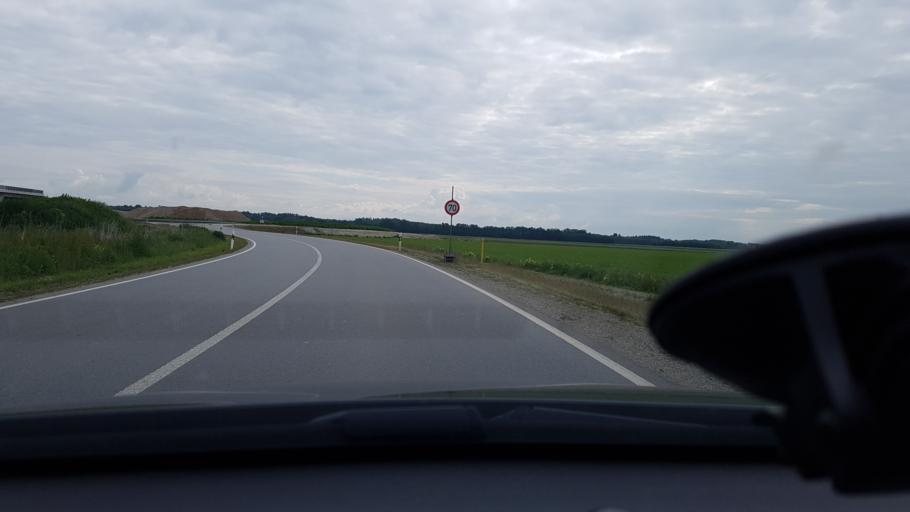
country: DE
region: Bavaria
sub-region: Lower Bavaria
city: Kirchham
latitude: 48.3524
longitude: 13.2529
